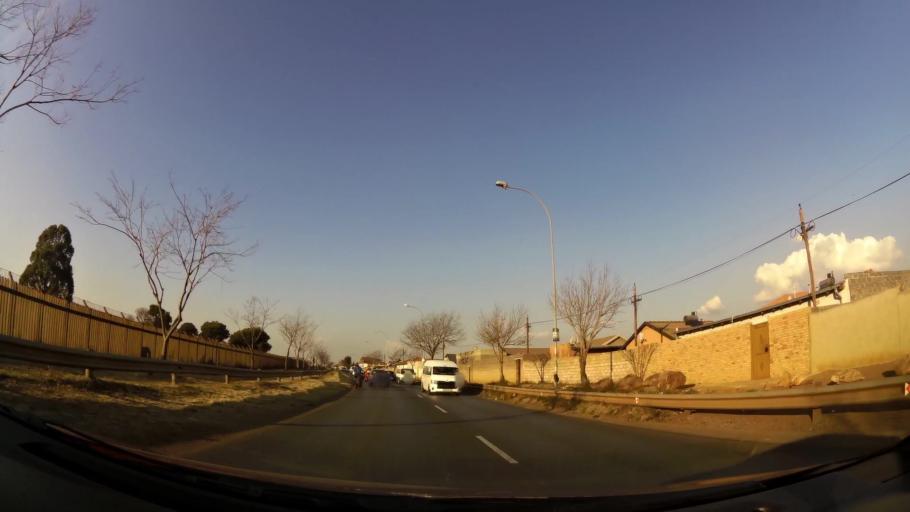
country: ZA
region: Gauteng
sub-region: City of Johannesburg Metropolitan Municipality
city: Soweto
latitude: -26.2306
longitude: 27.8458
